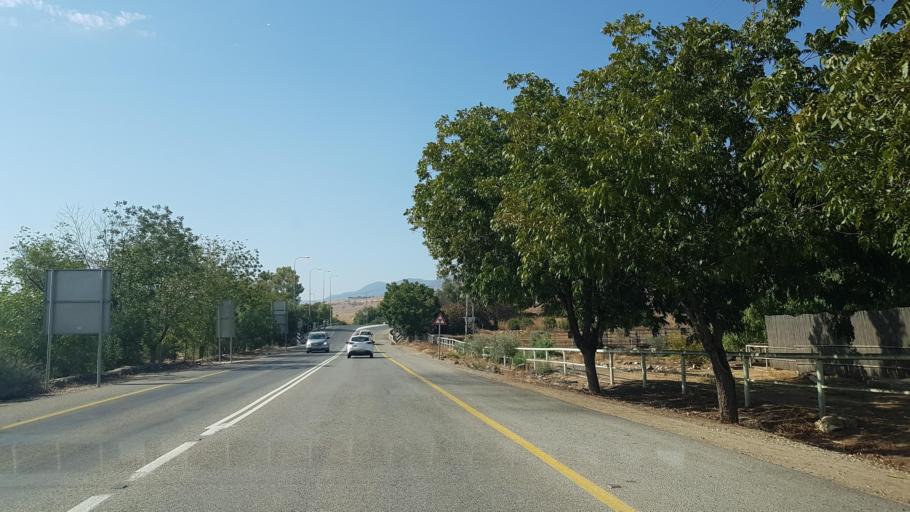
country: IL
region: Northern District
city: Rosh Pinna
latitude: 32.9041
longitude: 35.5500
